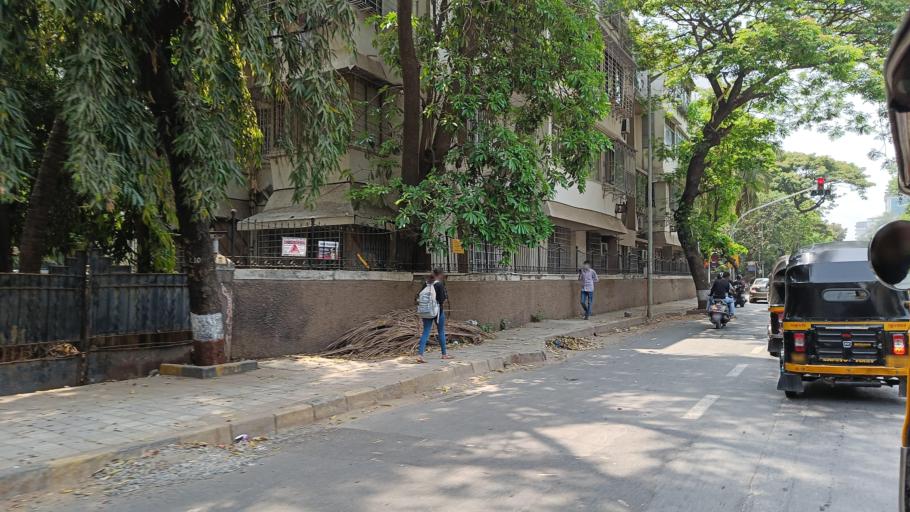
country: IN
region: Maharashtra
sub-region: Mumbai Suburban
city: Mumbai
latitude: 19.0791
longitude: 72.8344
